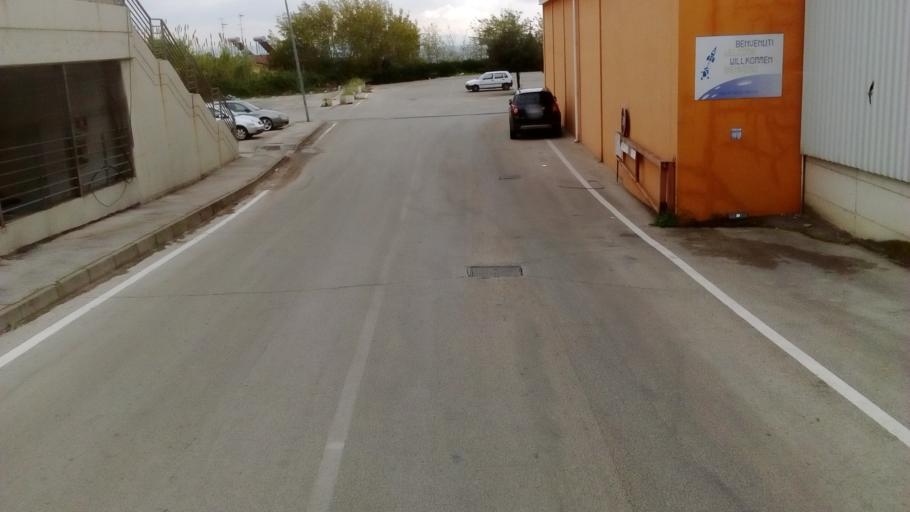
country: IT
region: Abruzzo
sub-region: Provincia di Chieti
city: Vasto
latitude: 42.0995
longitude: 14.7015
